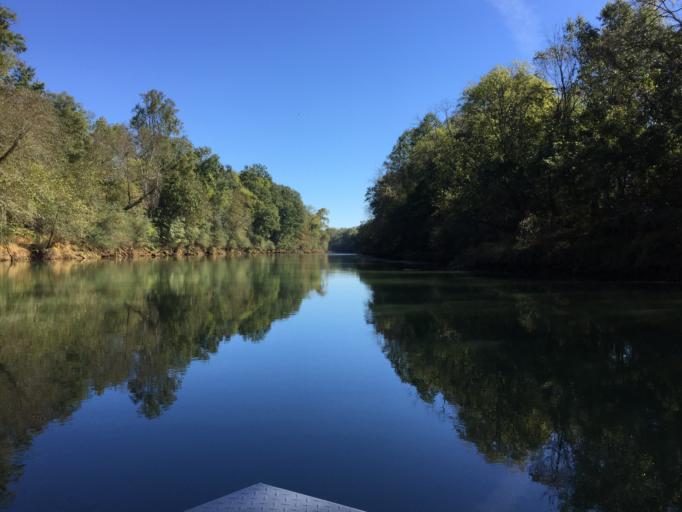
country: US
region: Georgia
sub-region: Gwinnett County
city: Duluth
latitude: 34.0305
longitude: -84.1396
